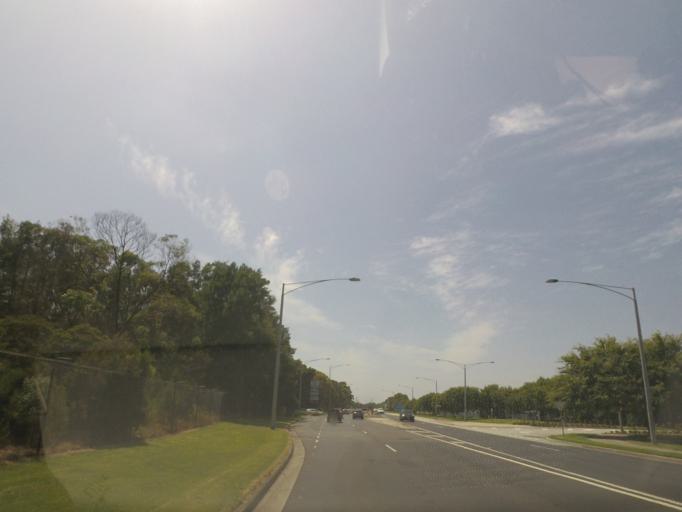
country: AU
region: Victoria
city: Heatherton
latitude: -37.9710
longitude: 145.1020
